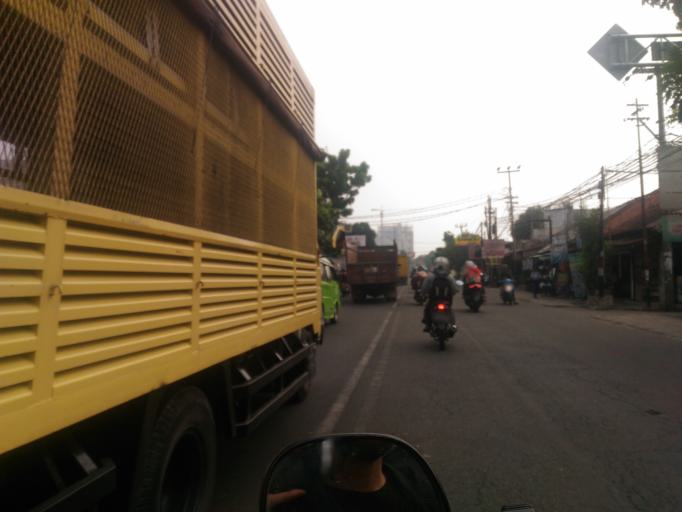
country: ID
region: West Java
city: Bogor
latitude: -6.5574
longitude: 106.8152
